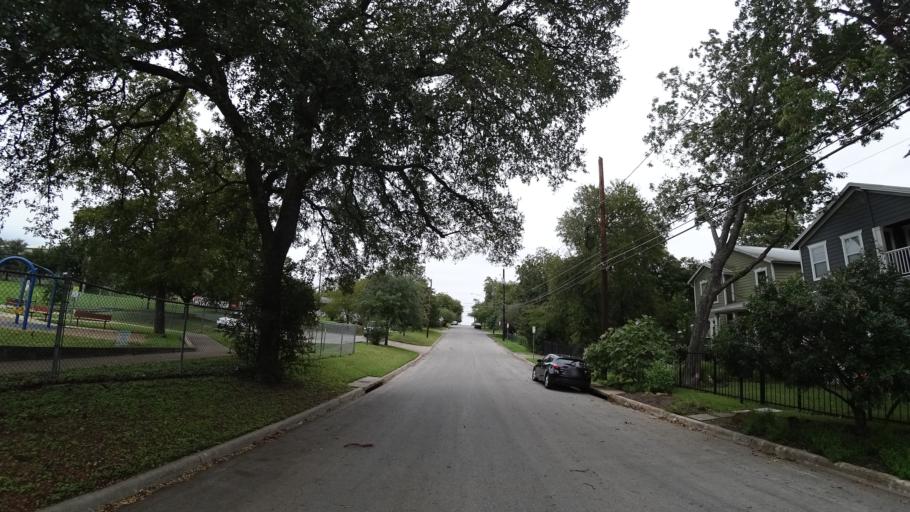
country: US
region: Texas
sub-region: Travis County
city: Austin
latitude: 30.2820
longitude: -97.7206
